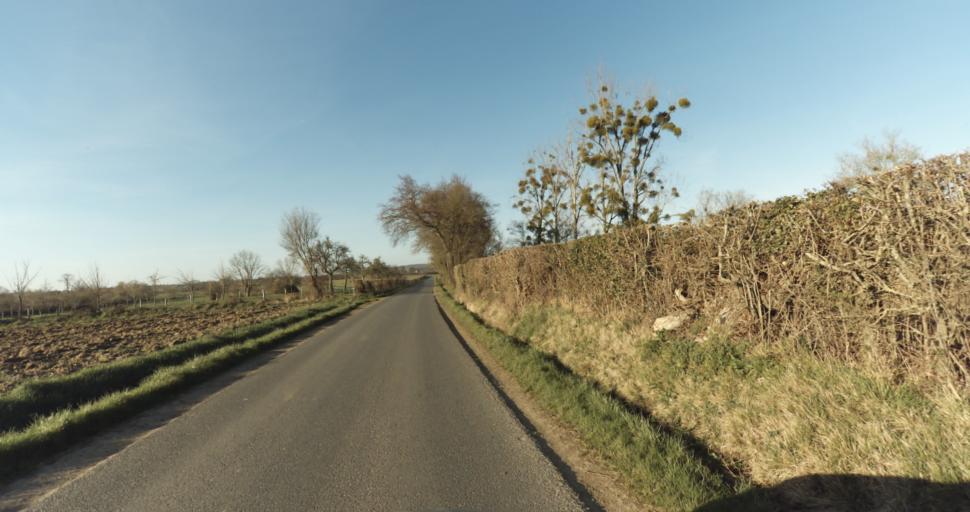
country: FR
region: Lower Normandy
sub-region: Departement de l'Orne
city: Trun
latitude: 48.9227
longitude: 0.0287
